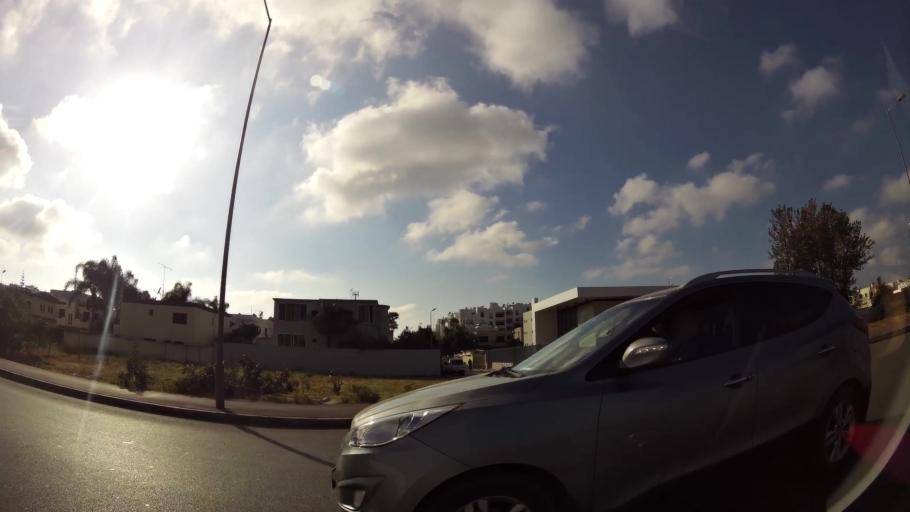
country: MA
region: Rabat-Sale-Zemmour-Zaer
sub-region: Skhirate-Temara
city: Temara
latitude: 33.9538
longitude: -6.8599
